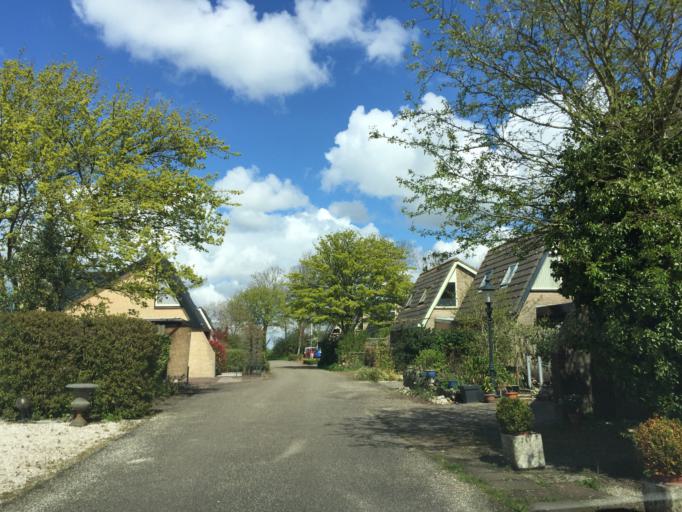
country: NL
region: South Holland
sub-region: Gemeente Leiderdorp
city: Leiderdorp
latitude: 52.1872
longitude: 4.5418
